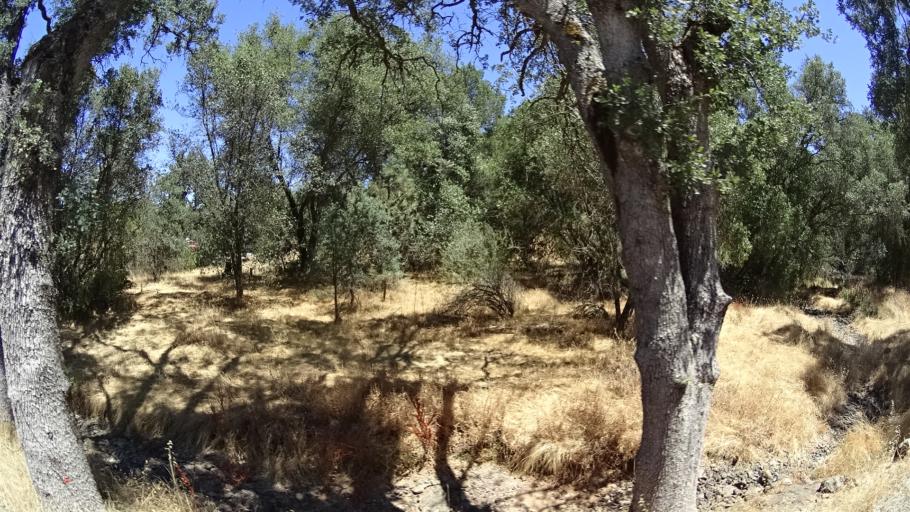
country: US
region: California
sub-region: Calaveras County
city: Copperopolis
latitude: 38.0611
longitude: -120.6541
